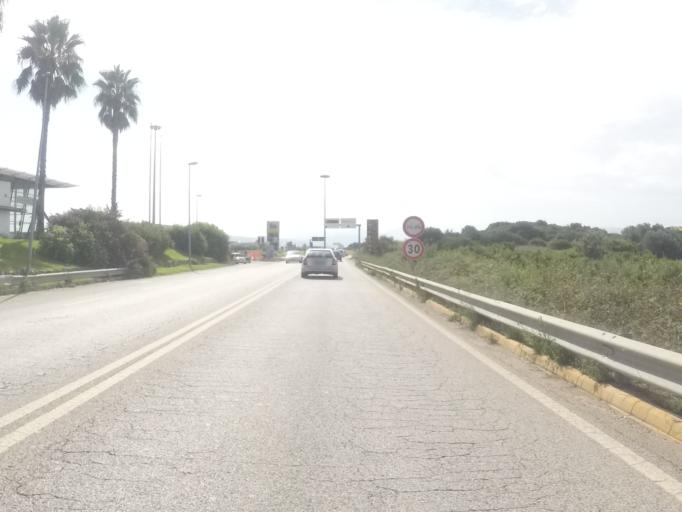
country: IT
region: Sardinia
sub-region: Provincia di Olbia-Tempio
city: Olbia
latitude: 40.9466
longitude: 9.5027
